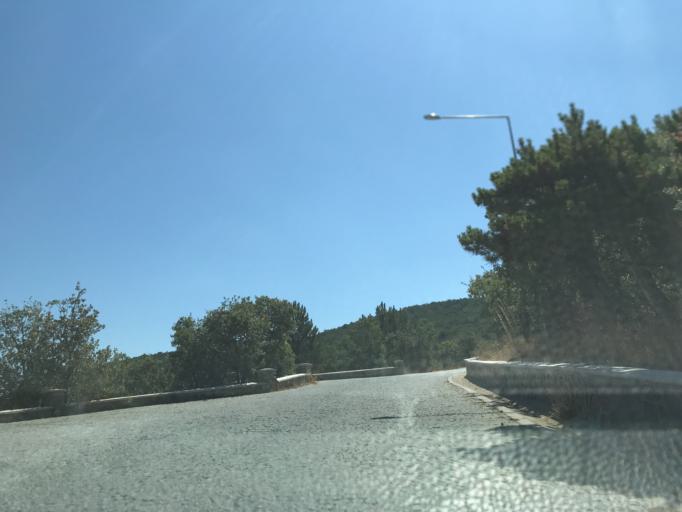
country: TR
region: Yozgat
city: Yozgat
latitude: 39.8094
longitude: 34.8075
